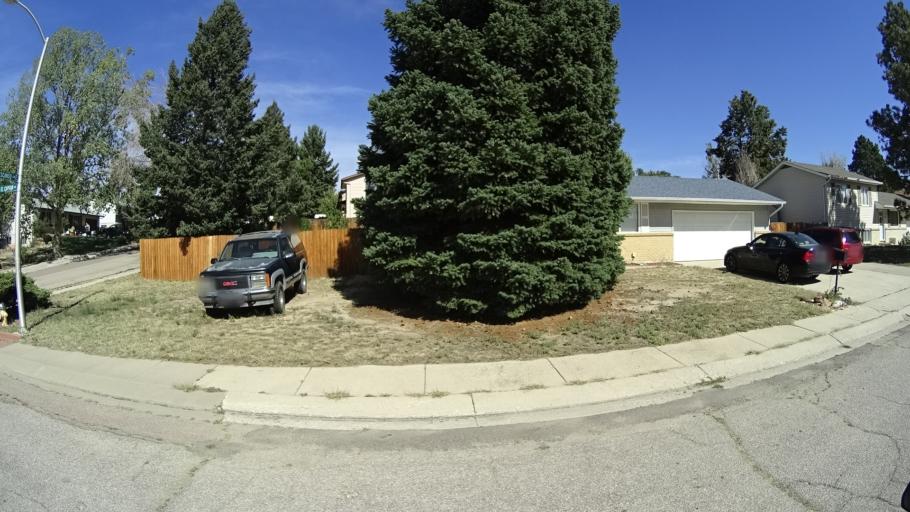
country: US
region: Colorado
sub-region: El Paso County
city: Colorado Springs
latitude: 38.9081
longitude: -104.7770
